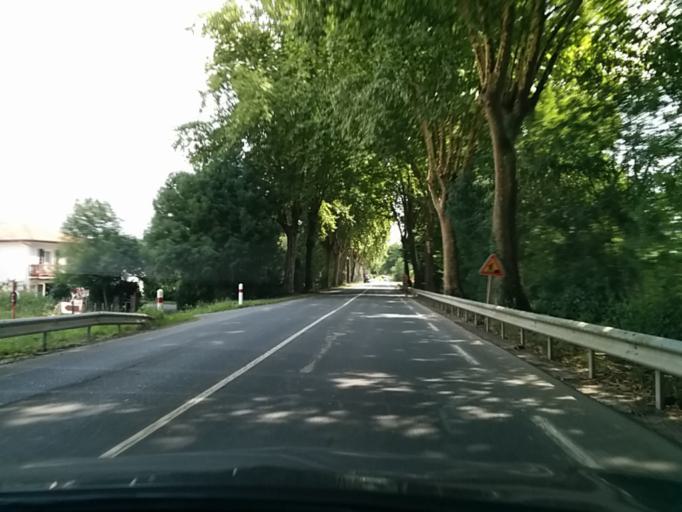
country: FR
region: Aquitaine
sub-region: Departement des Pyrenees-Atlantiques
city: Urrugne
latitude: 43.3615
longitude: -1.6968
